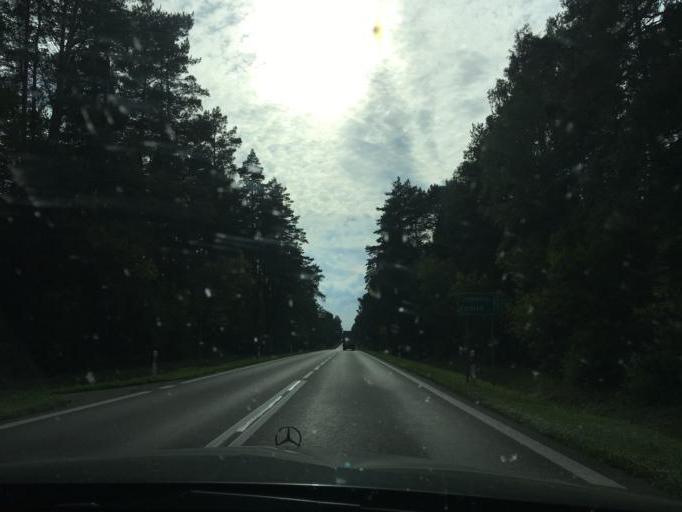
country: PL
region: Podlasie
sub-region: Powiat grajewski
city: Rajgrod
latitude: 53.7004
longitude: 22.6555
